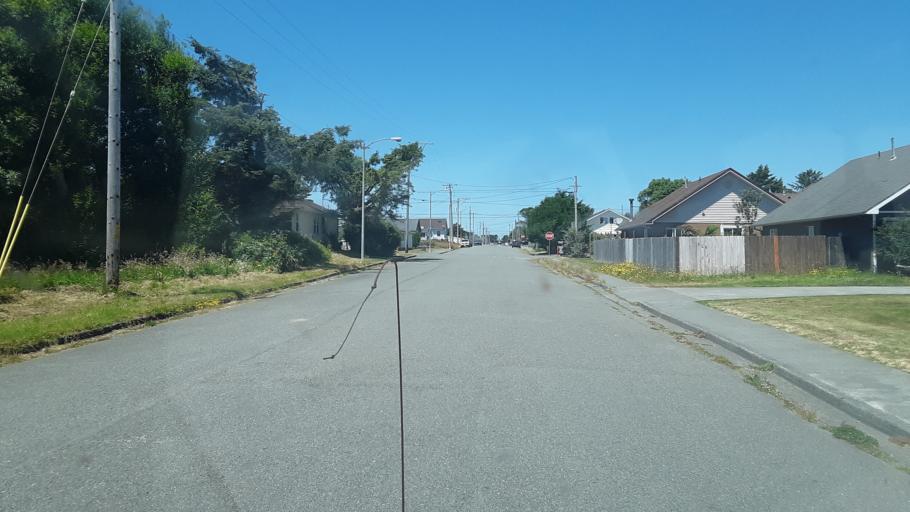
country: US
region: California
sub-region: Del Norte County
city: Crescent City
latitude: 41.7494
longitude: -124.2032
